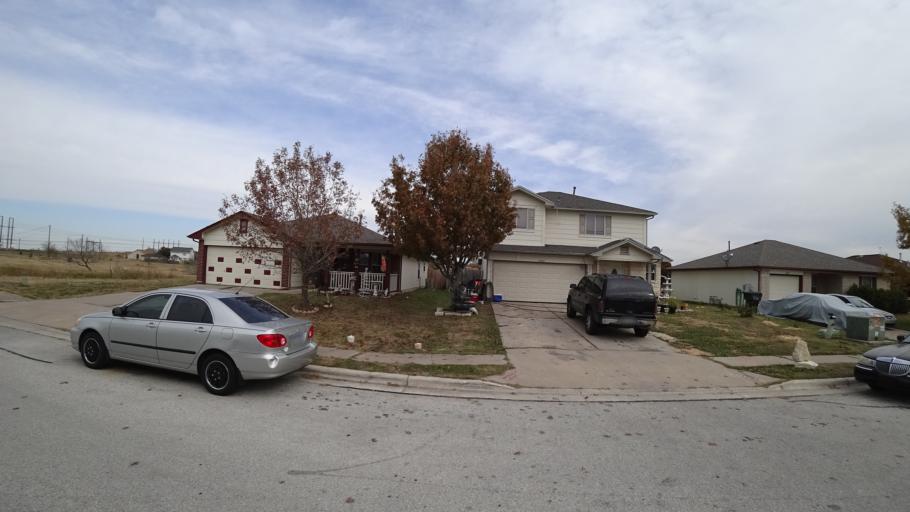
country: US
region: Texas
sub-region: Travis County
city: Garfield
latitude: 30.1566
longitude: -97.6505
